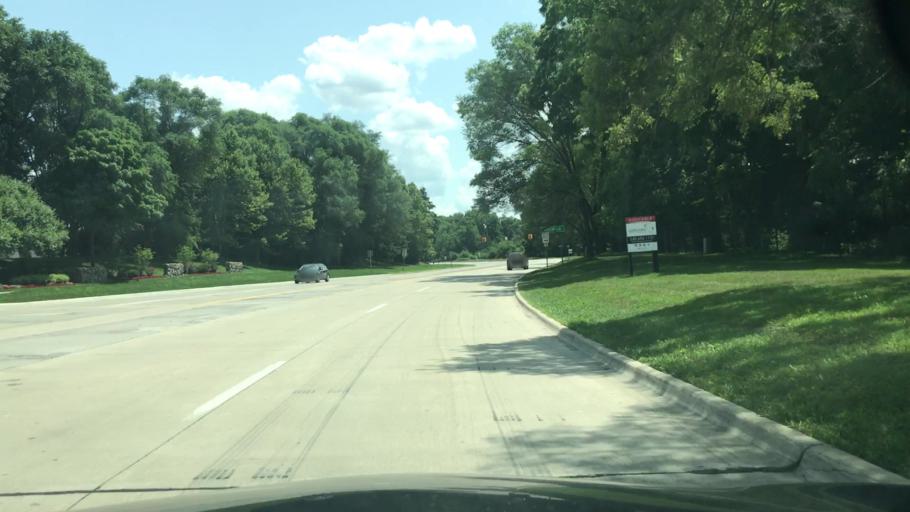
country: US
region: Michigan
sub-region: Wayne County
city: Northville
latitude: 42.4395
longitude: -83.4708
